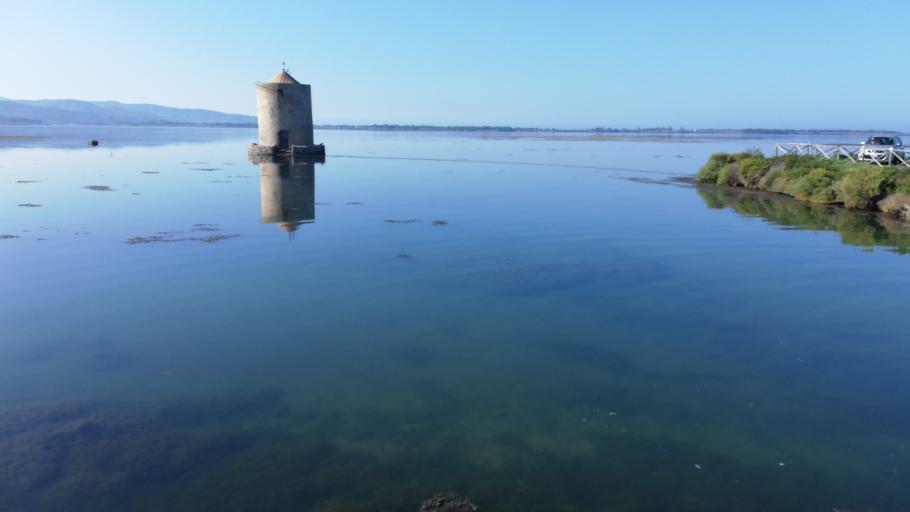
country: IT
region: Tuscany
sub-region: Provincia di Grosseto
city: Orbetello
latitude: 42.4357
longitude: 11.2059
